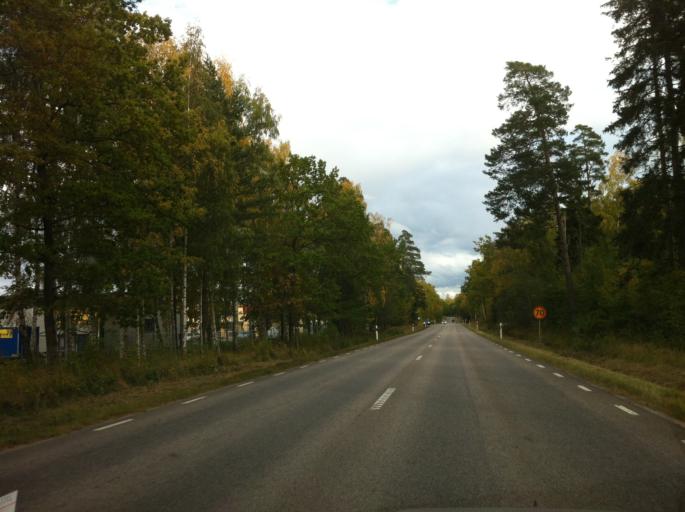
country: SE
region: OEstergoetland
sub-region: Motala Kommun
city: Motala
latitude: 58.5241
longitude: 15.0239
